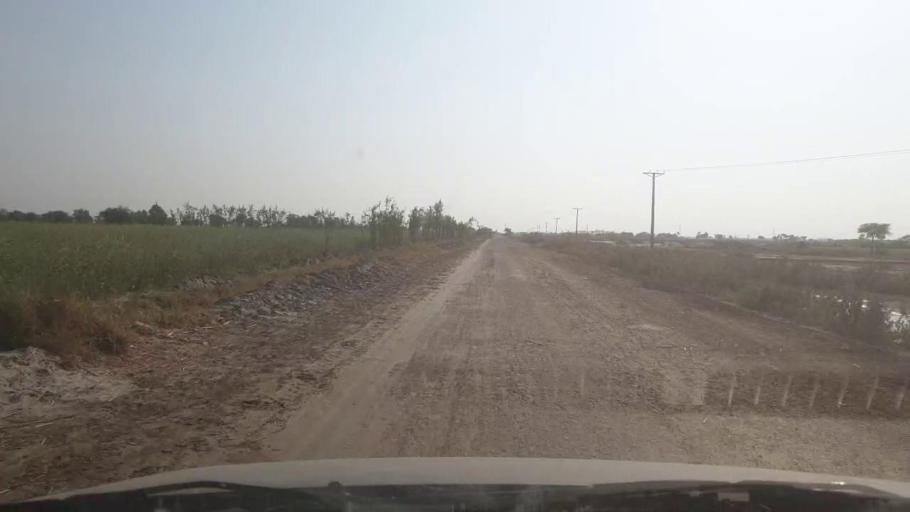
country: PK
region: Sindh
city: Samaro
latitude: 25.1514
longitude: 69.3826
